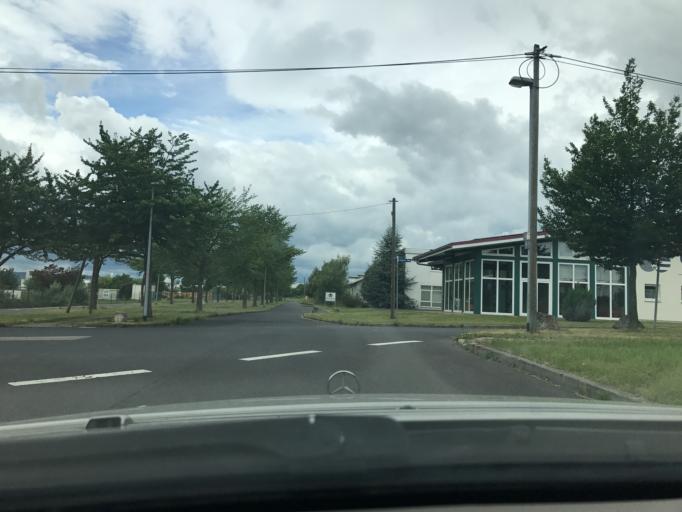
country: DE
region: Thuringia
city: Muehlhausen
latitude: 51.1954
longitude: 10.4815
